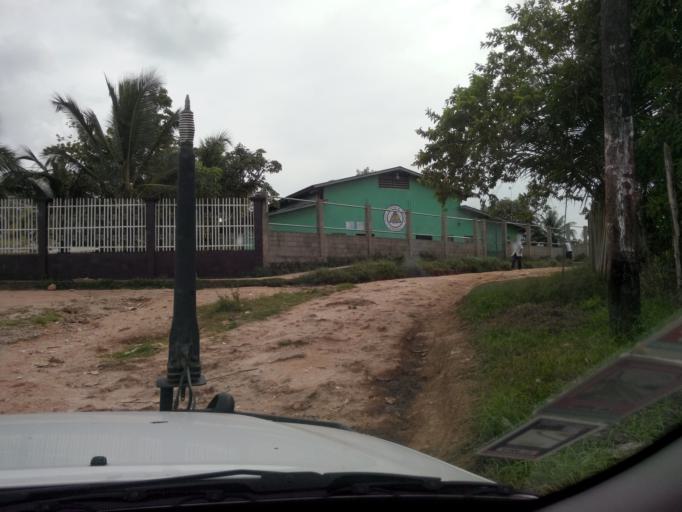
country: NI
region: Atlantico Sur
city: Bluefields
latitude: 12.0275
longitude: -83.7709
